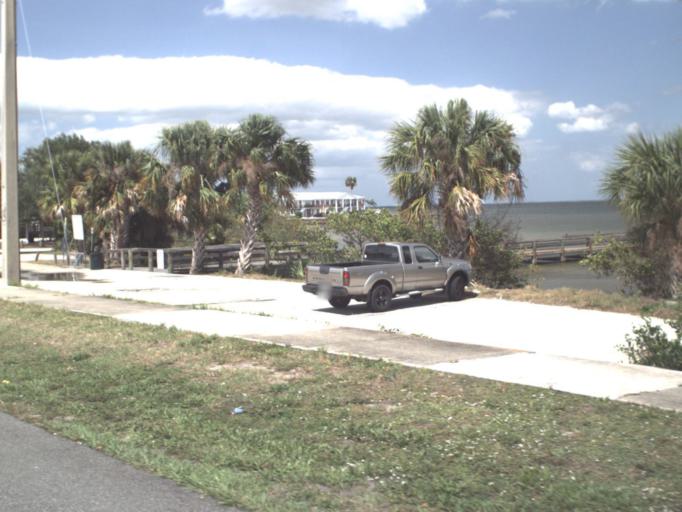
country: US
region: Florida
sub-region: Brevard County
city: Titusville
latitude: 28.5656
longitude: -80.7983
